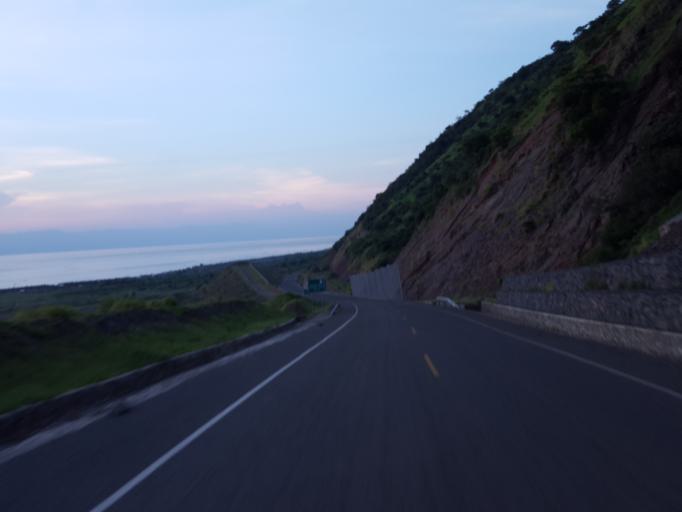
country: UG
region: Western Region
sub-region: Kibale District
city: Kagadi
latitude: 1.2457
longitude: 30.7586
